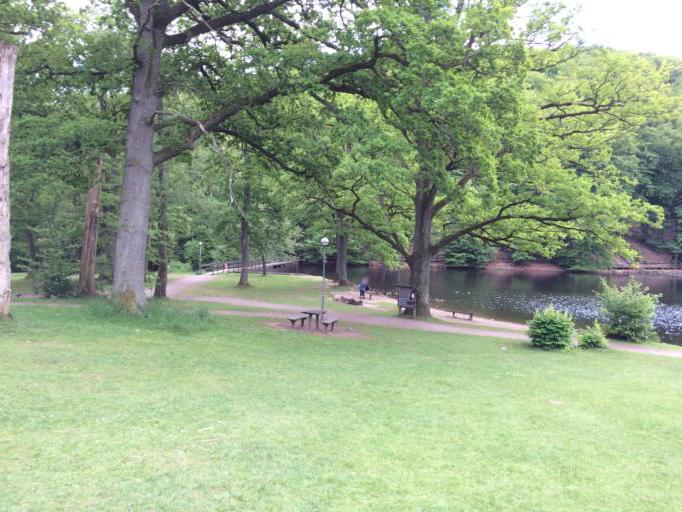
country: SE
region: Skane
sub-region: Klippans Kommun
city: Ljungbyhed
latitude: 56.0385
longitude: 13.2510
